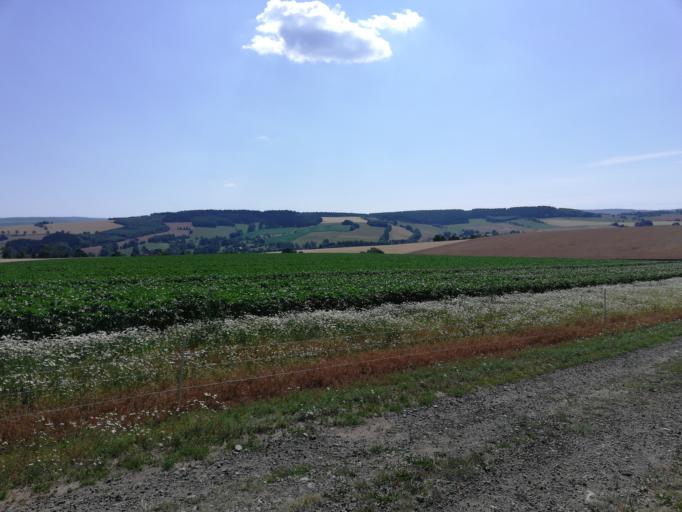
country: DE
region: Saxony
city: Sayda
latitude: 50.7342
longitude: 13.4386
